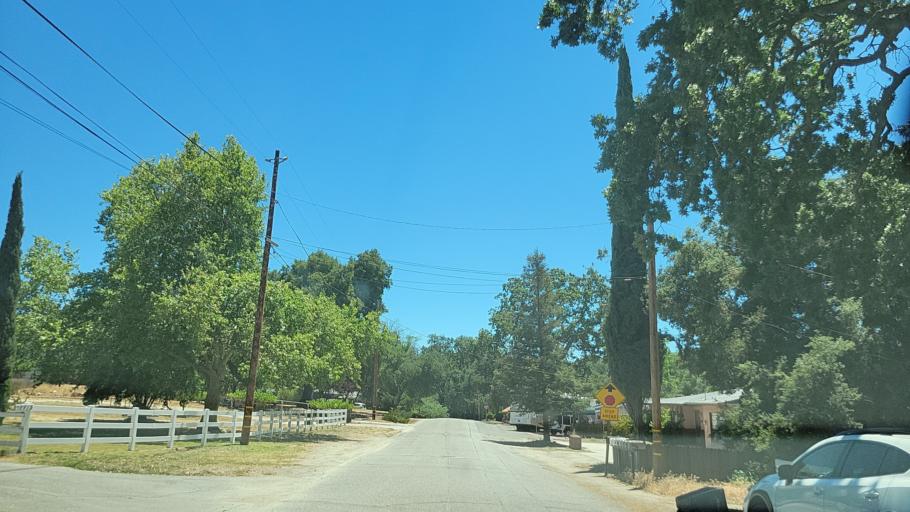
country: US
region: California
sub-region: San Luis Obispo County
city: Atascadero
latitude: 35.4731
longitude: -120.6635
